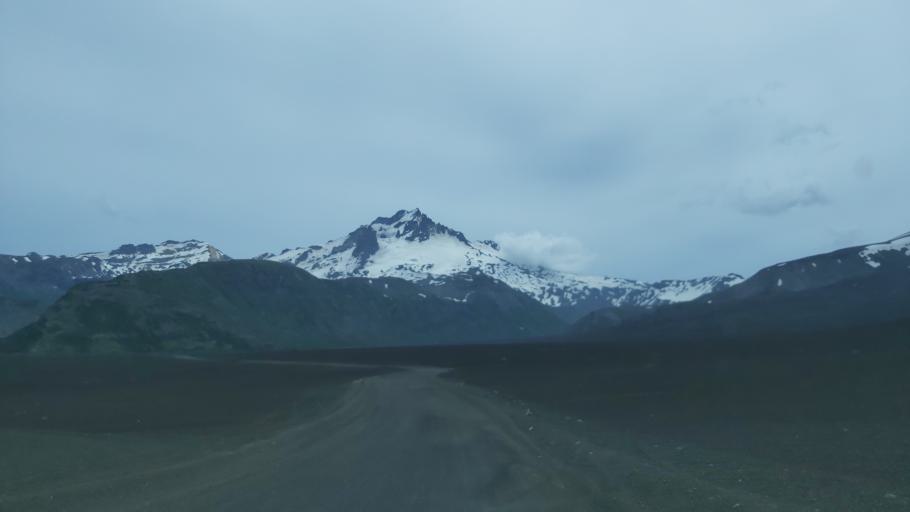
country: AR
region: Neuquen
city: Andacollo
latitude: -37.4582
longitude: -71.3006
